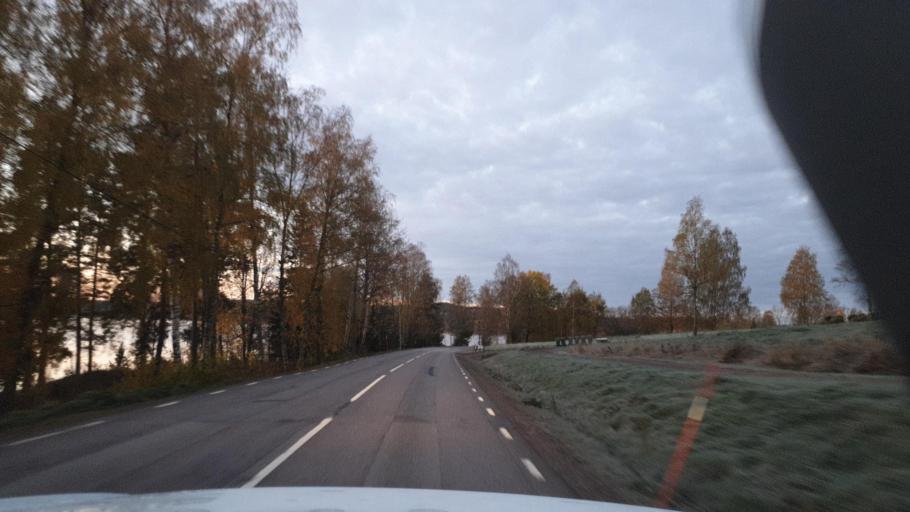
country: SE
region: Vaermland
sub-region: Eda Kommun
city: Charlottenberg
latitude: 59.8132
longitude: 12.2576
